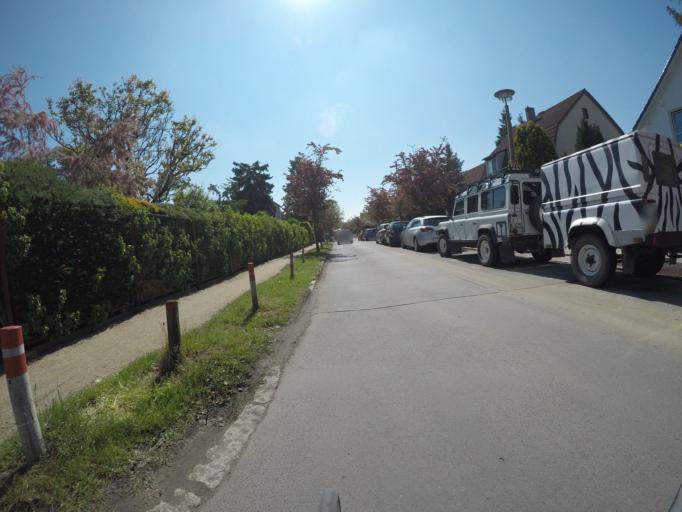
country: DE
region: Berlin
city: Fennpfuhl
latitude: 52.5385
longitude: 13.4540
